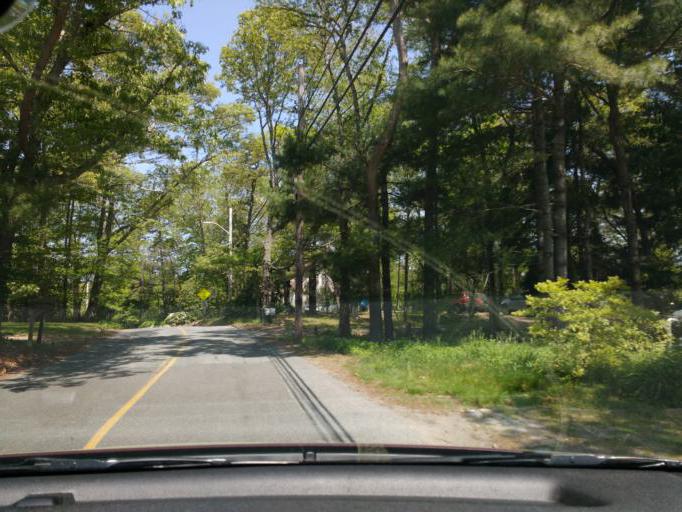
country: US
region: Massachusetts
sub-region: Barnstable County
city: East Falmouth
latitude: 41.5993
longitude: -70.5792
